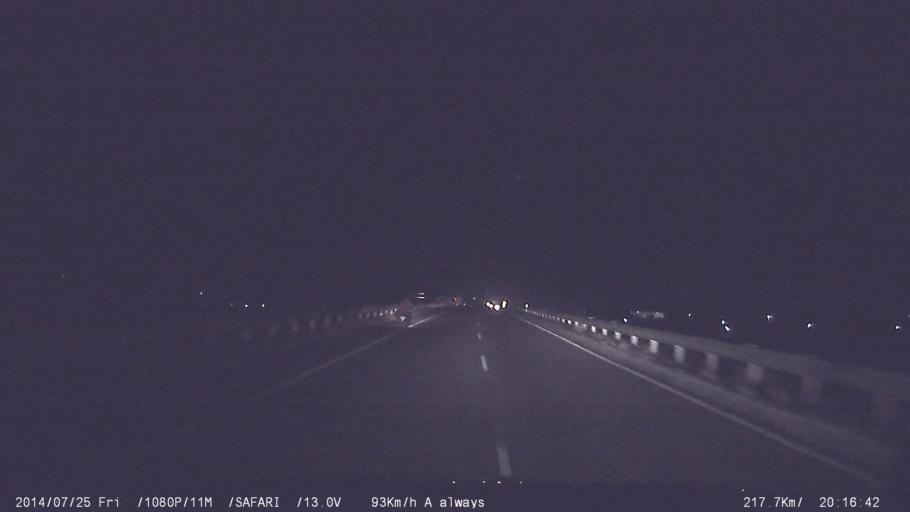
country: IN
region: Tamil Nadu
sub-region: Salem
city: Ilampillai
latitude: 11.5442
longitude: 77.9817
